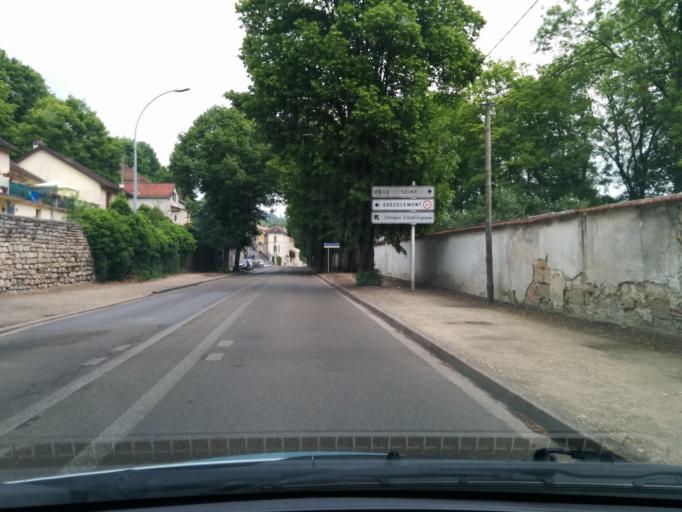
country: FR
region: Ile-de-France
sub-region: Departement des Yvelines
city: Meulan-en-Yvelines
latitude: 49.0079
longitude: 1.9286
